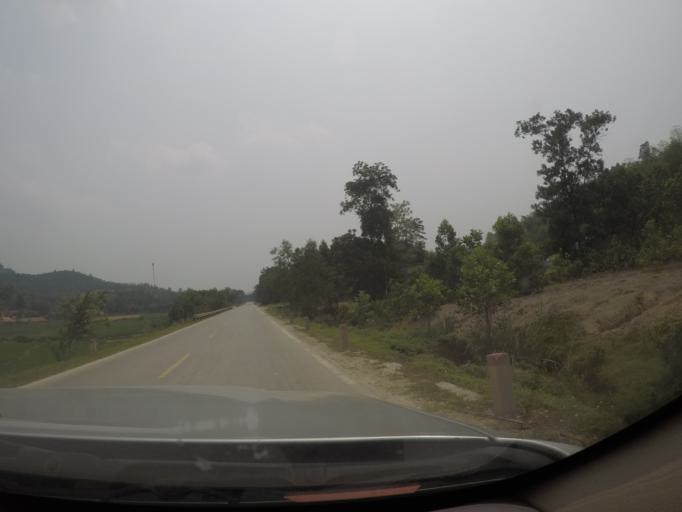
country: VN
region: Thanh Hoa
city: Thi Tran Yen Cat
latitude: 19.7780
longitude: 105.4058
